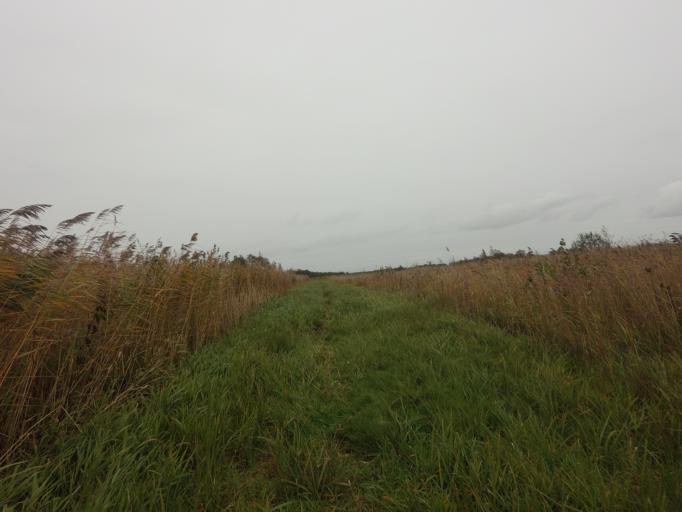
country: NL
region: Overijssel
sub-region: Gemeente Steenwijkerland
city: Oldemarkt
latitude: 52.7782
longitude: 5.9647
